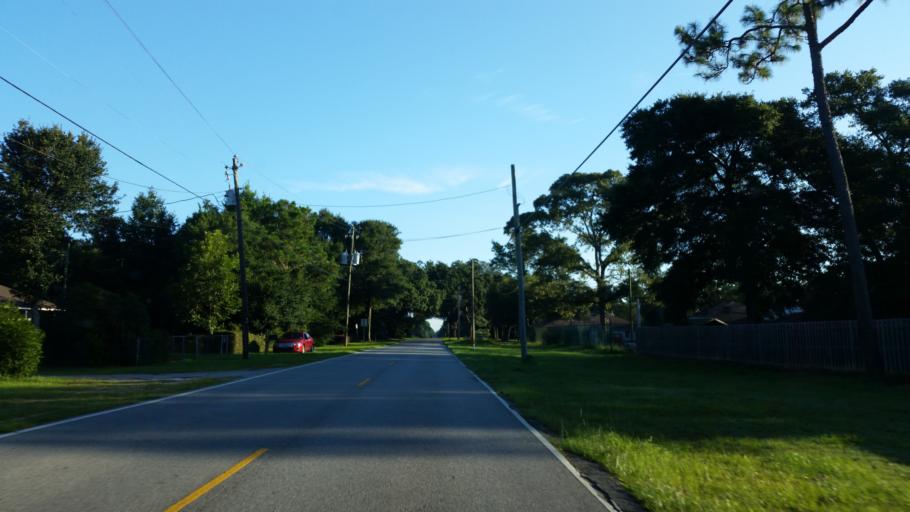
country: US
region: Florida
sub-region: Escambia County
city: Bellview
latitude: 30.5041
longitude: -87.3227
